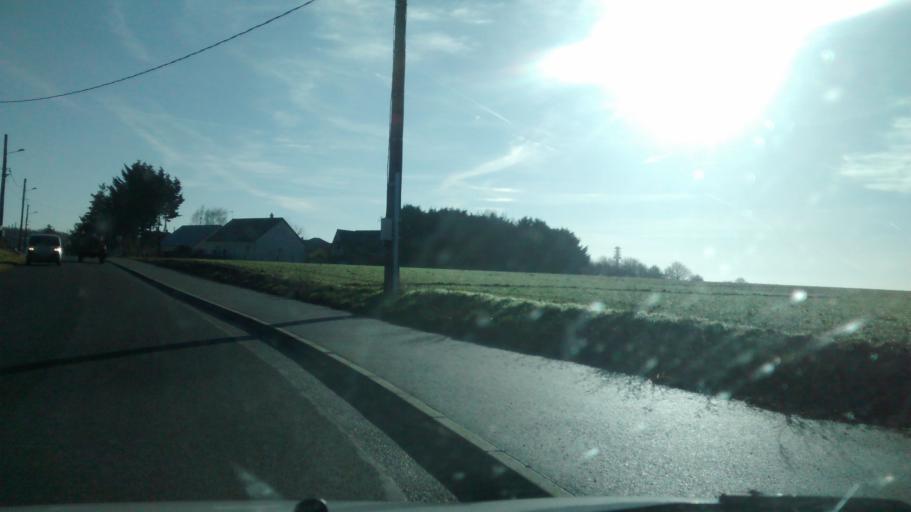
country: FR
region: Centre
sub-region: Departement d'Indre-et-Loire
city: Monnaie
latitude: 47.4986
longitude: 0.7950
